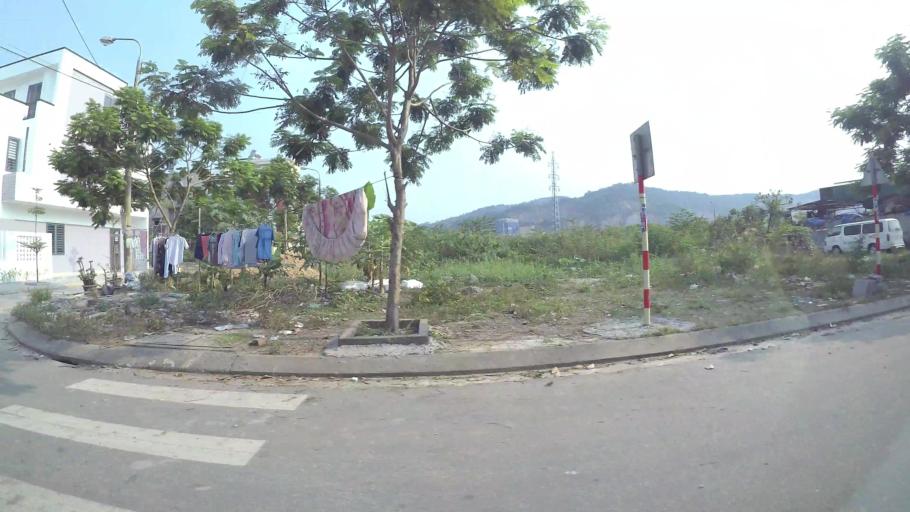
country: VN
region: Da Nang
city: Lien Chieu
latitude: 16.0520
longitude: 108.1660
